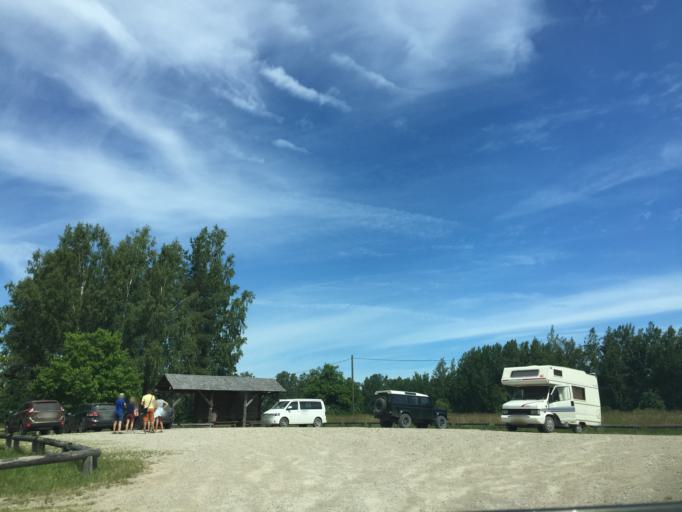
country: LV
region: Dundaga
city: Dundaga
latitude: 57.6263
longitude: 22.2921
